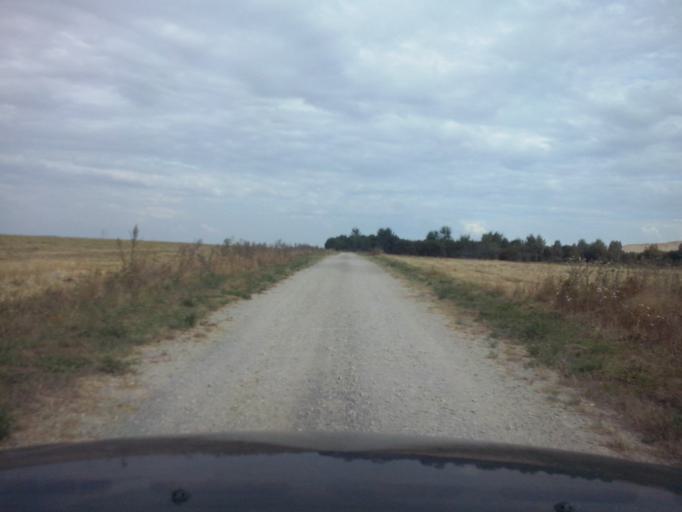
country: PL
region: Swietokrzyskie
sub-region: Powiat kielecki
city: Lagow
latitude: 50.7856
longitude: 21.0844
